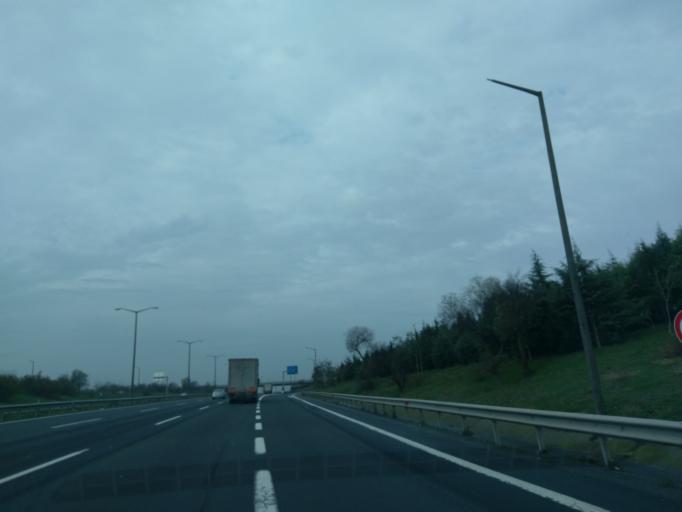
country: TR
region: Istanbul
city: Buyukcavuslu
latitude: 41.1917
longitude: 28.0887
